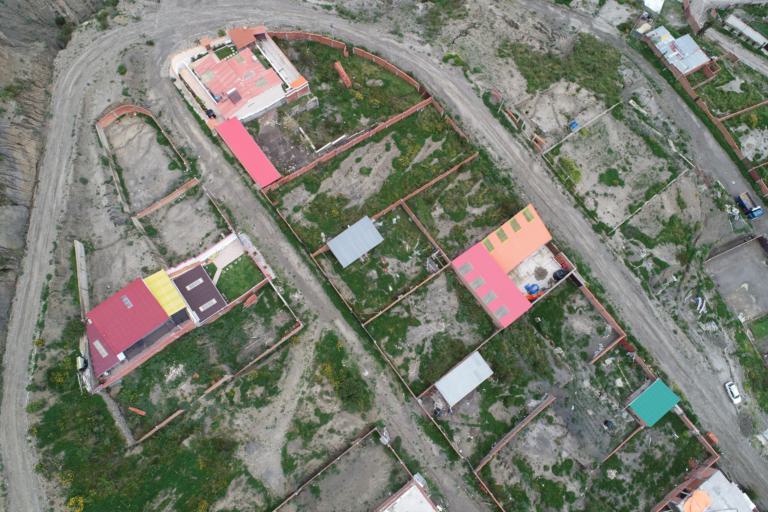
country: BO
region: La Paz
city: La Paz
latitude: -16.4977
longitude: -68.0794
